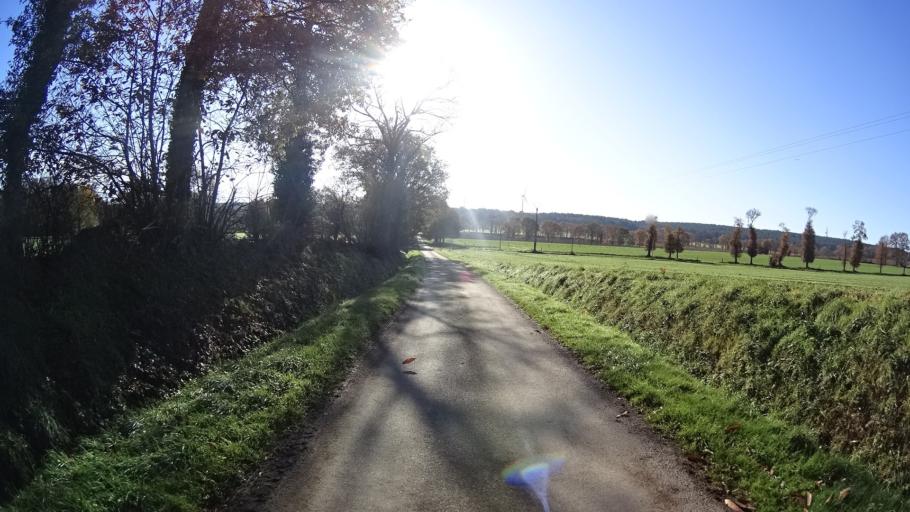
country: FR
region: Brittany
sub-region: Departement du Morbihan
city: Saint-Martin-sur-Oust
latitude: 47.7871
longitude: -2.1985
